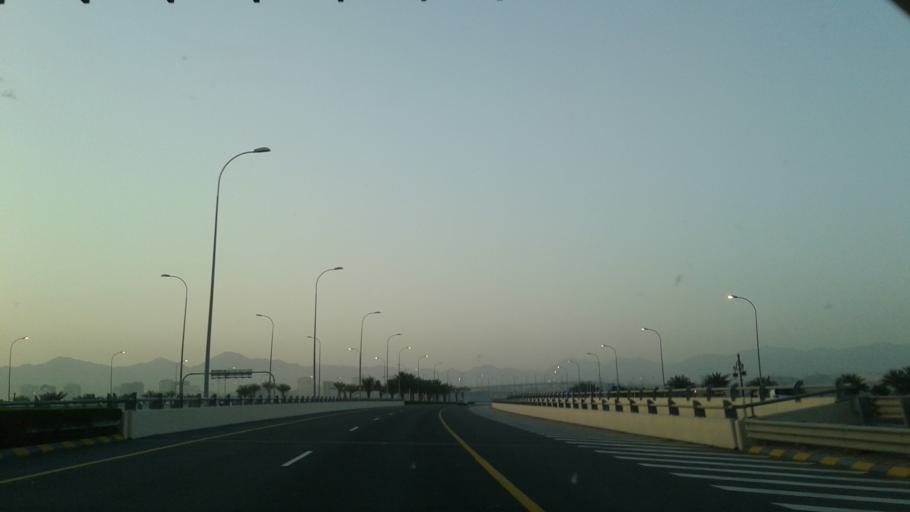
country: OM
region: Muhafazat Masqat
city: Bawshar
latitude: 23.5939
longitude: 58.3318
